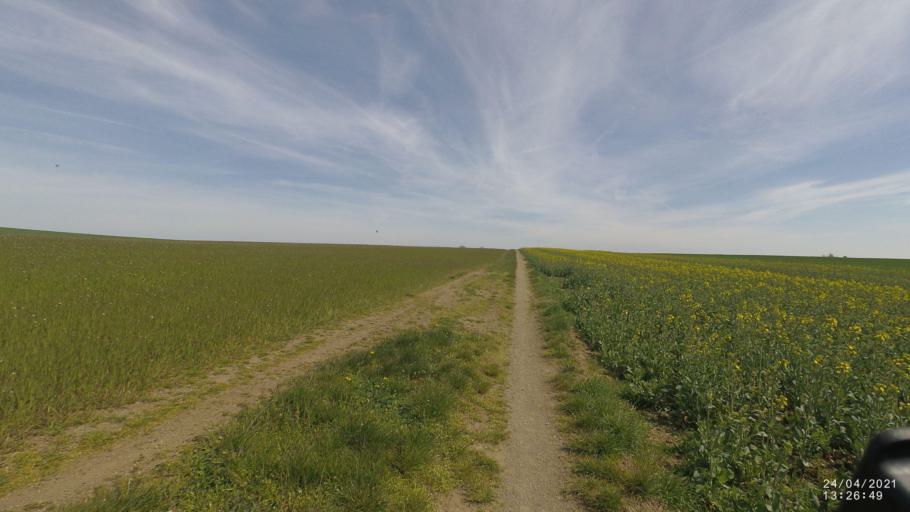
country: DE
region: Rheinland-Pfalz
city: Trimbs
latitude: 50.3318
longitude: 7.2952
